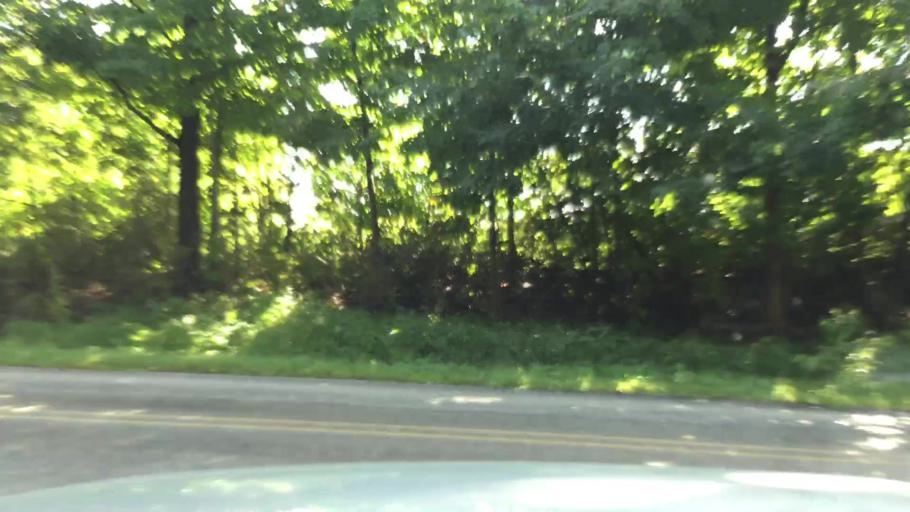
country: US
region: Michigan
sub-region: Lenawee County
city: Hudson
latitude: 41.8724
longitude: -84.4202
